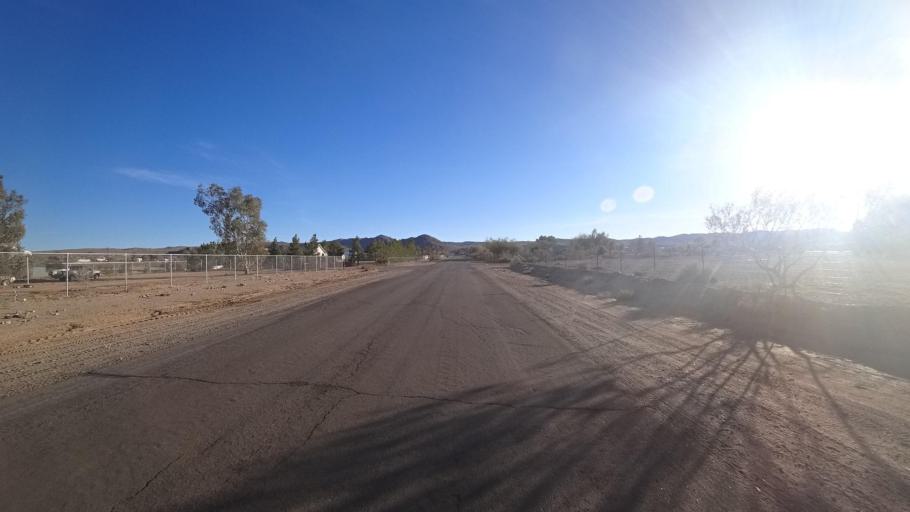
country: US
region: California
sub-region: Kern County
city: Ridgecrest
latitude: 35.5978
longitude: -117.6616
